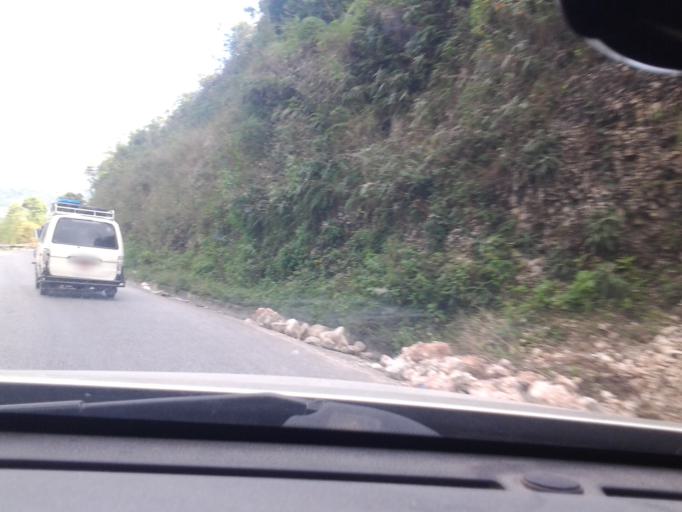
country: HT
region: Sud-Est
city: Jacmel
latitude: 18.3003
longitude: -72.5811
